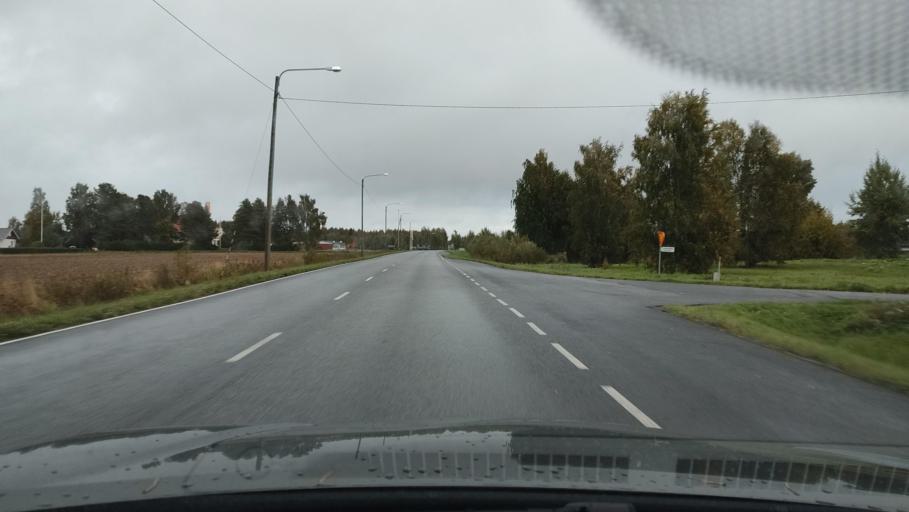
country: FI
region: Ostrobothnia
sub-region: Sydosterbotten
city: Kristinestad
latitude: 62.2646
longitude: 21.4794
